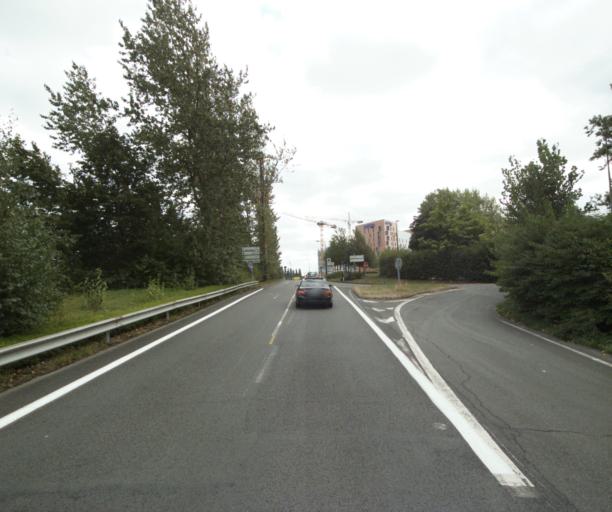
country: FR
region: Nord-Pas-de-Calais
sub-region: Departement du Nord
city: Lezennes
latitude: 50.6150
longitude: 3.1349
